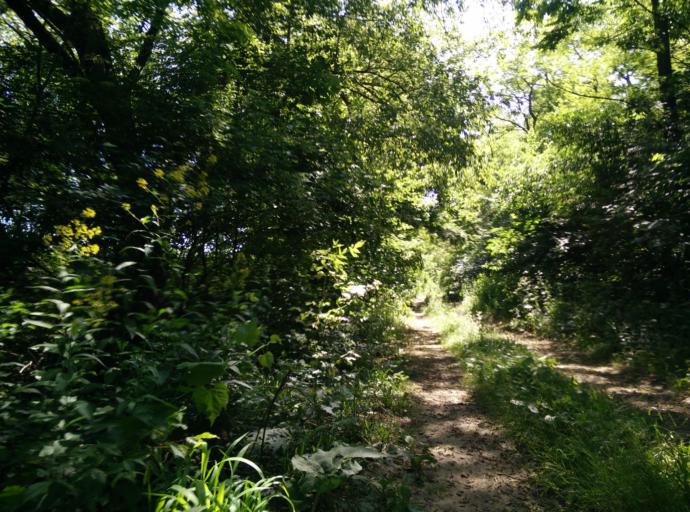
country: HU
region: Pest
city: Biatorbagy
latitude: 47.4709
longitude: 18.8500
